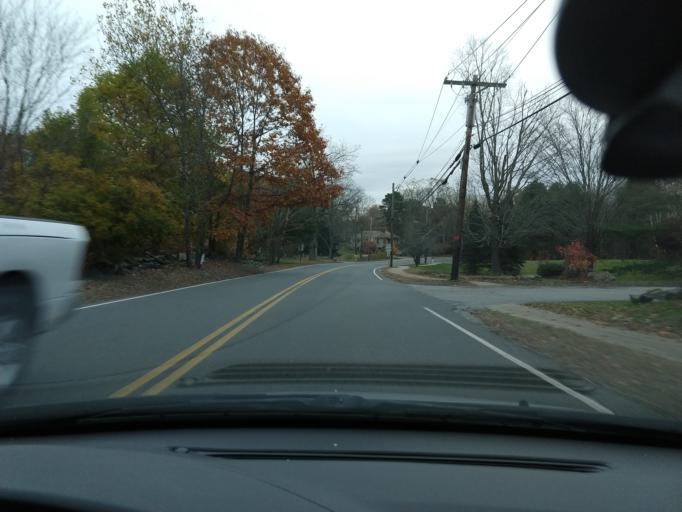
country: US
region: Massachusetts
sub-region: Middlesex County
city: Carlisle
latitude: 42.5292
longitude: -71.3461
